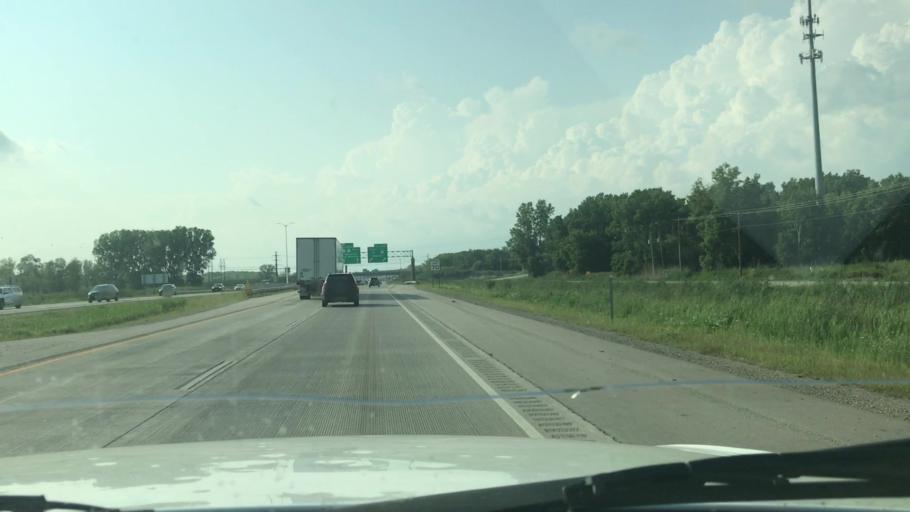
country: US
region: Wisconsin
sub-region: Brown County
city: Green Bay
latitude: 44.5490
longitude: -88.0375
